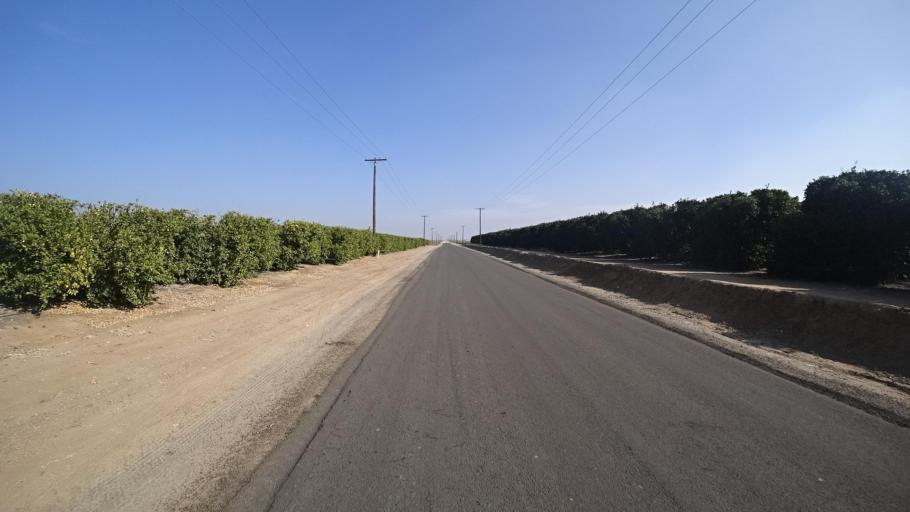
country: US
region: California
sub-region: Kern County
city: McFarland
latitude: 35.6311
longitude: -119.1755
